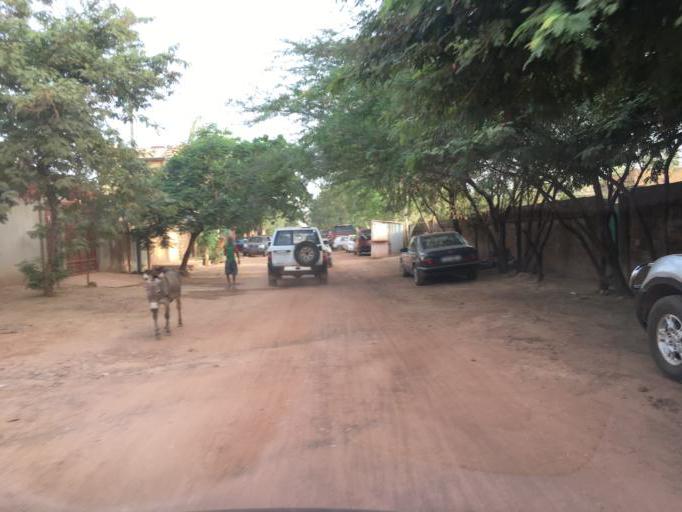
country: BF
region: Centre
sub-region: Kadiogo Province
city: Ouagadougou
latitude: 12.3675
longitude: -1.4990
